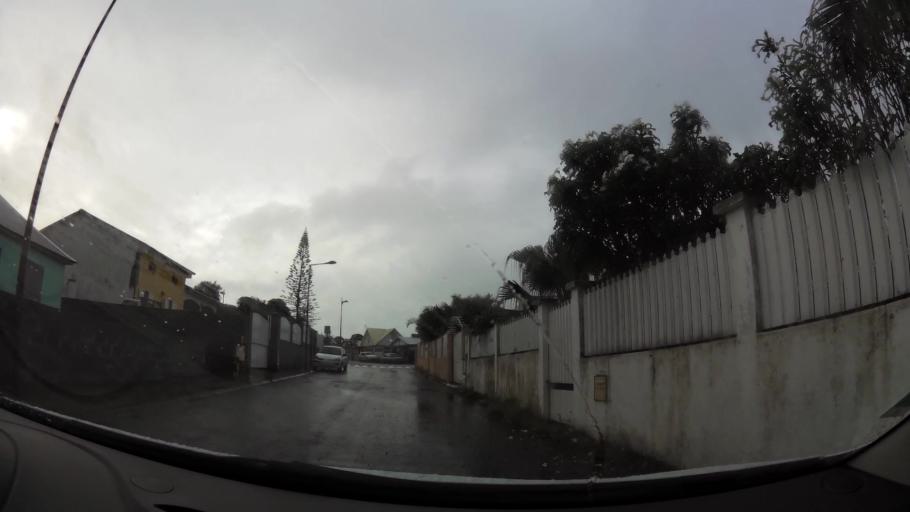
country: RE
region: Reunion
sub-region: Reunion
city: Saint-Andre
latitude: -20.9787
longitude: 55.6600
